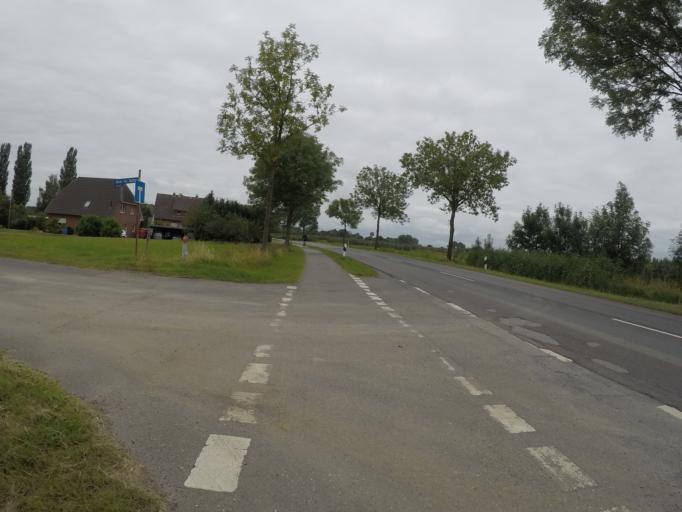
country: DE
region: Lower Saxony
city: Jork
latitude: 53.5385
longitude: 9.7002
